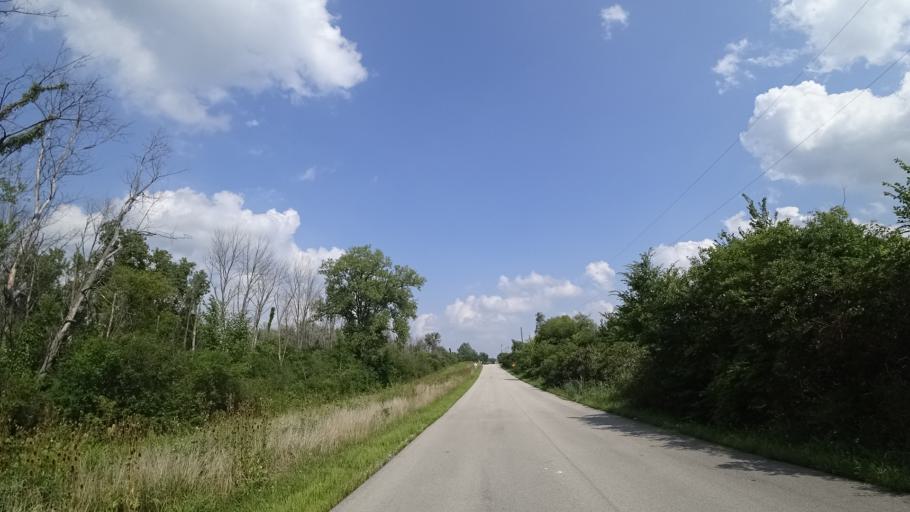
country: US
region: Illinois
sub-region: Will County
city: Goodings Grove
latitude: 41.6442
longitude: -87.8954
